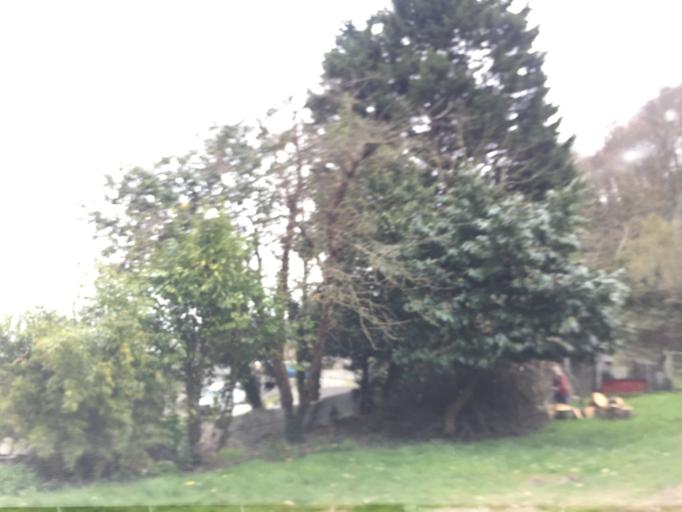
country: FR
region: Brittany
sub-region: Departement d'Ille-et-Vilaine
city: Saint-Broladre
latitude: 48.5901
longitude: -1.6336
